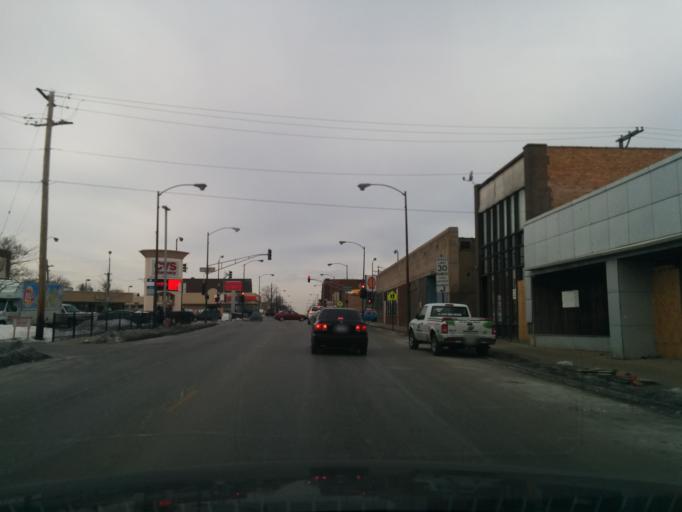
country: US
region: Illinois
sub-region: Cook County
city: Elmwood Park
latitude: 41.9384
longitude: -87.7850
